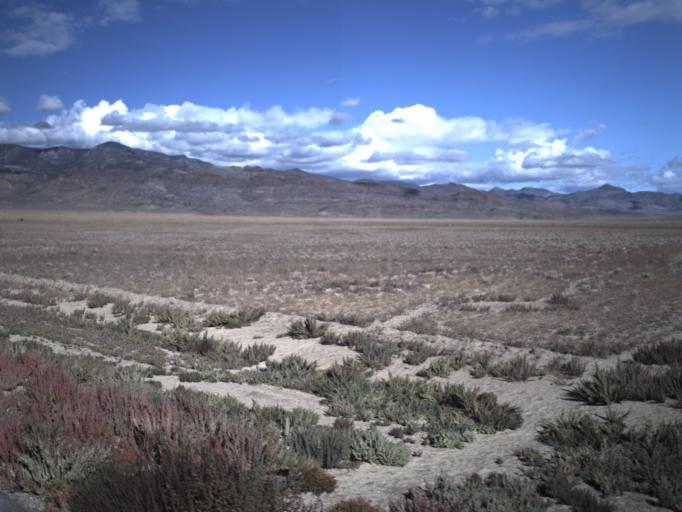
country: US
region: Utah
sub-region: Beaver County
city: Milford
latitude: 38.4797
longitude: -113.4351
